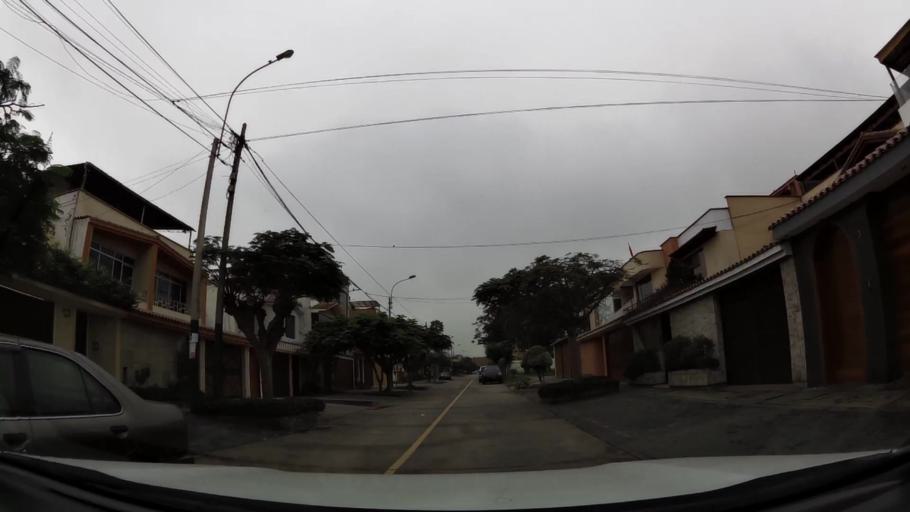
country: PE
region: Lima
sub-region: Lima
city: Surco
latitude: -12.1350
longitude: -77.0028
